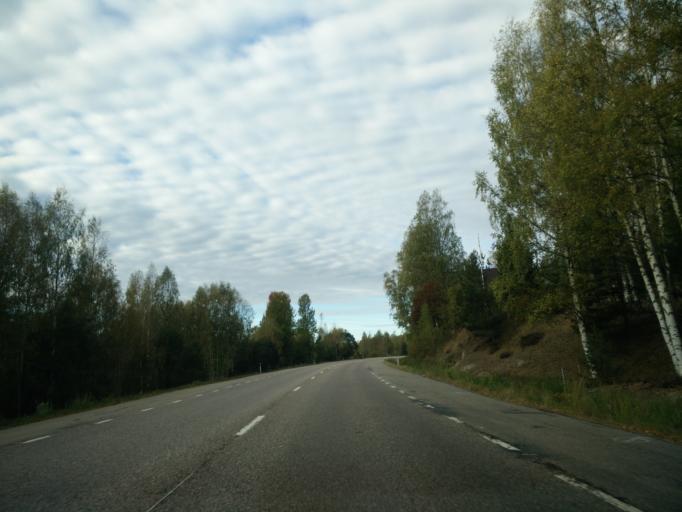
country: SE
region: Gaevleborg
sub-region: Soderhamns Kommun
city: Soderhamn
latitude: 61.2875
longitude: 16.9929
